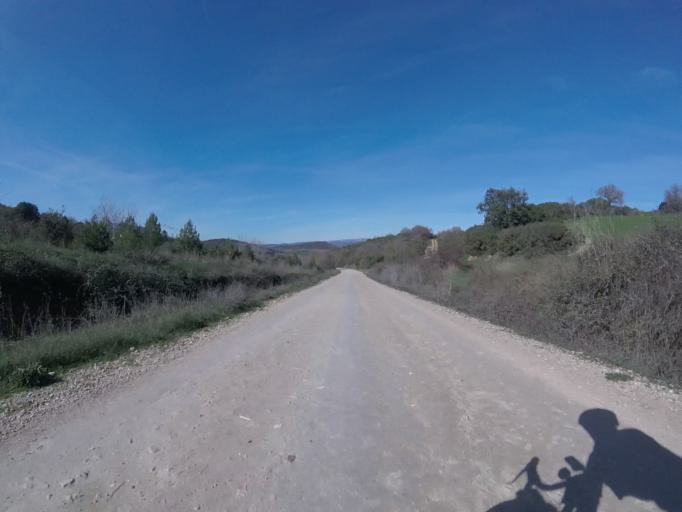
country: ES
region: Navarre
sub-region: Provincia de Navarra
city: Oteiza
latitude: 42.6453
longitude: -1.9609
